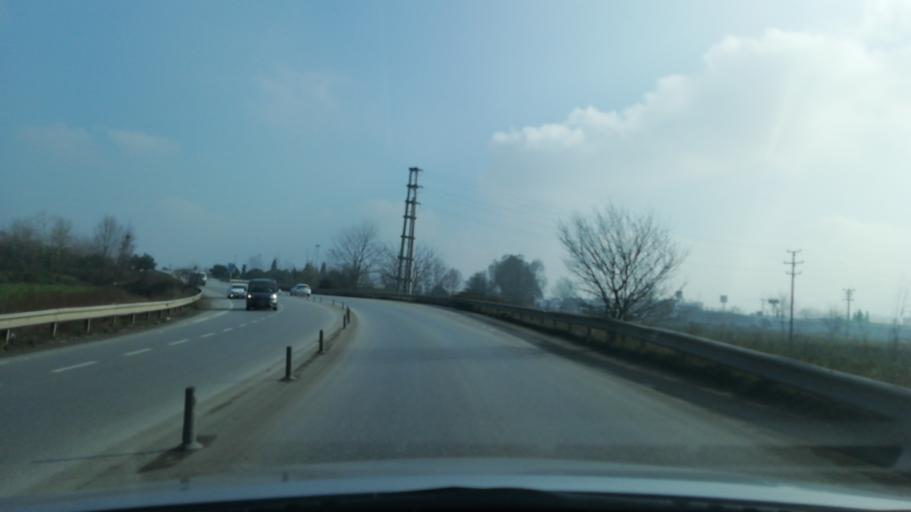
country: TR
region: Sakarya
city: Adapazari
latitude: 40.7275
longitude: 30.3793
